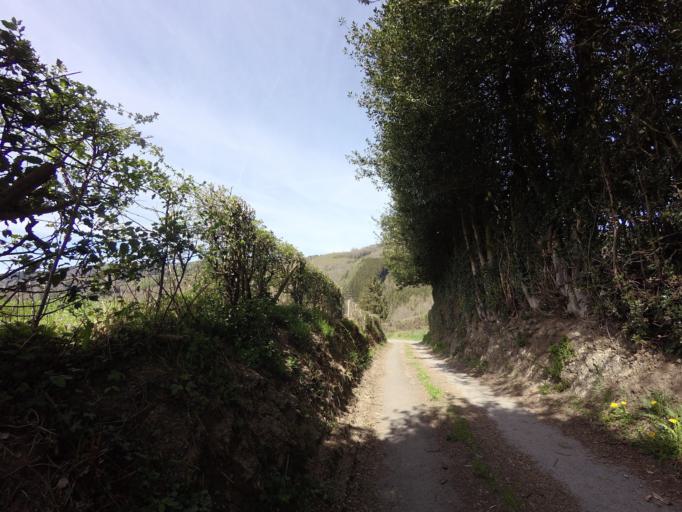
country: BE
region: Wallonia
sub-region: Province de Liege
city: Trois-Ponts
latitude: 50.4206
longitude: 5.8771
